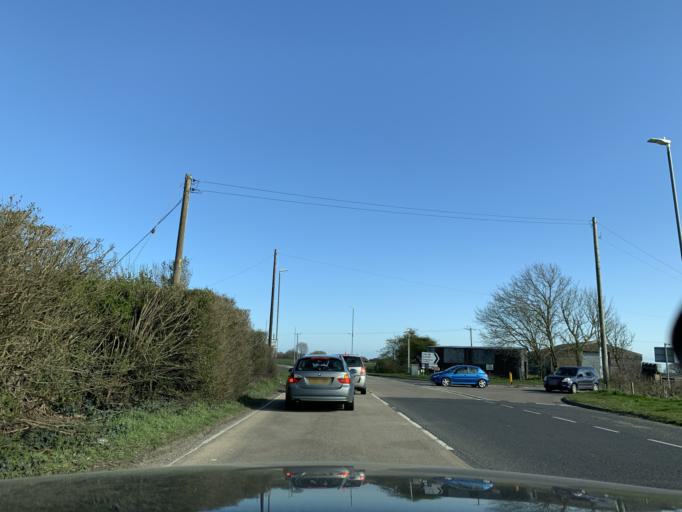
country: GB
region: England
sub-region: Kent
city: New Romney
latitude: 50.9850
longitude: 0.9214
